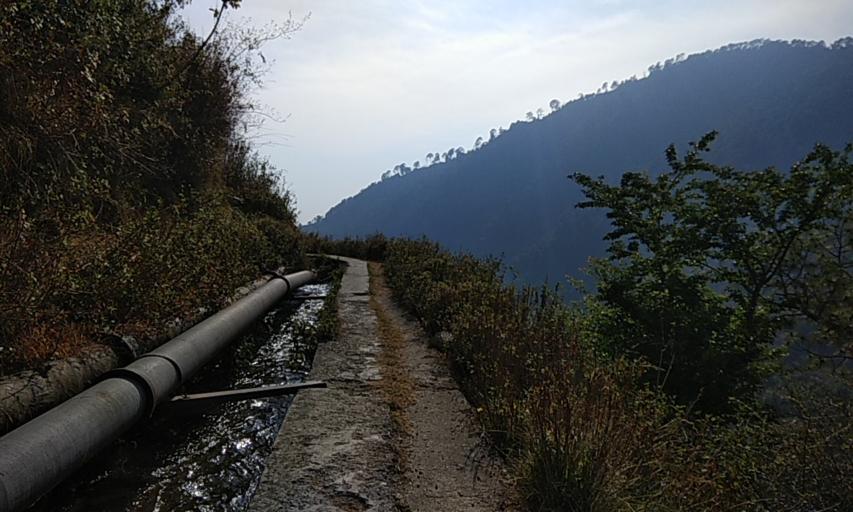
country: IN
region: Himachal Pradesh
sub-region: Kangra
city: Palampur
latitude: 32.1431
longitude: 76.5392
